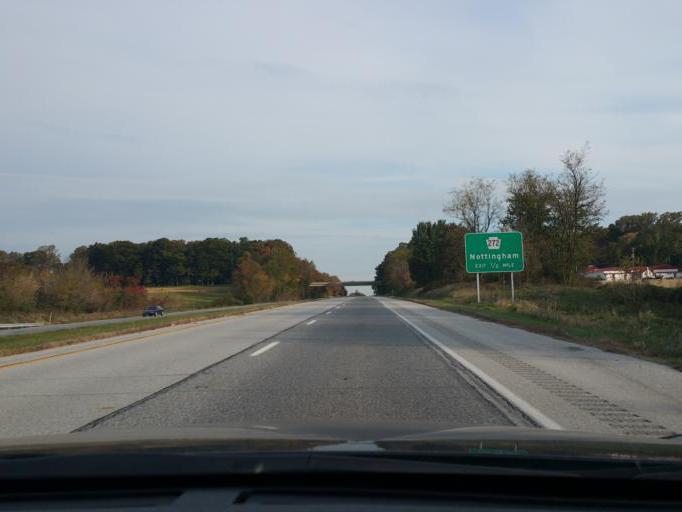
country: US
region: Maryland
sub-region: Cecil County
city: Rising Sun
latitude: 39.7392
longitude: -76.0243
